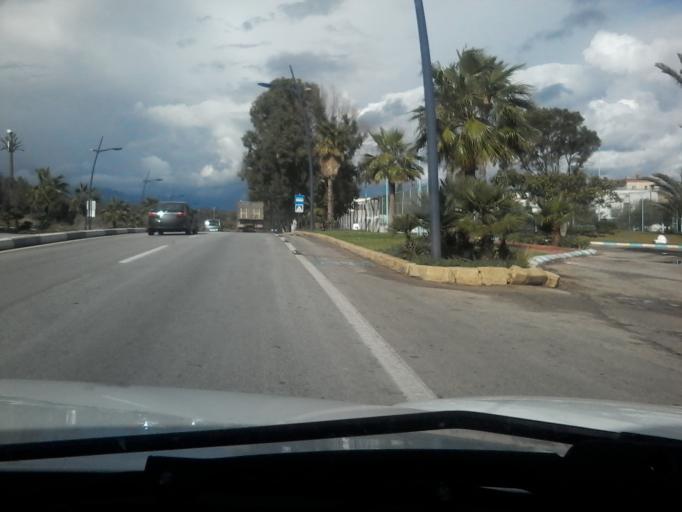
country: ES
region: Ceuta
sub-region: Ceuta
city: Ceuta
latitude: 35.7604
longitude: -5.3484
